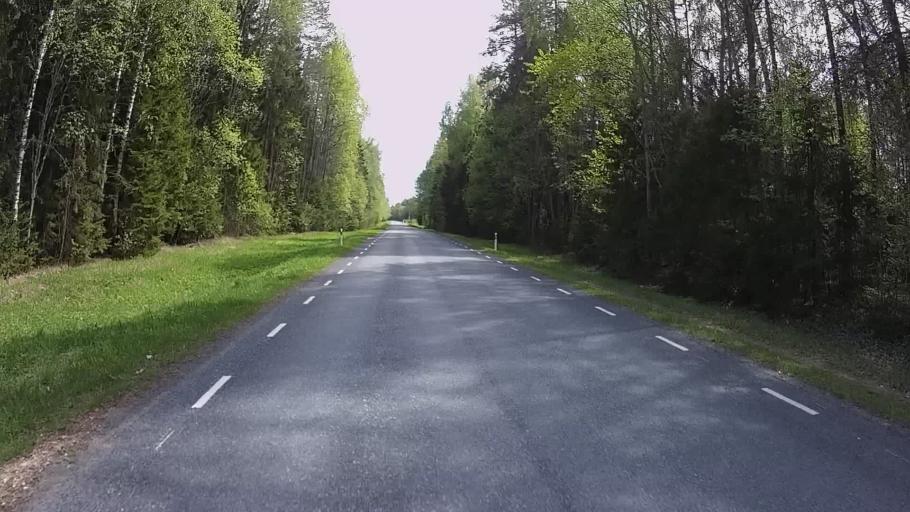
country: EE
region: Valgamaa
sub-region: Valga linn
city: Valga
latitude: 57.7027
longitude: 26.2429
